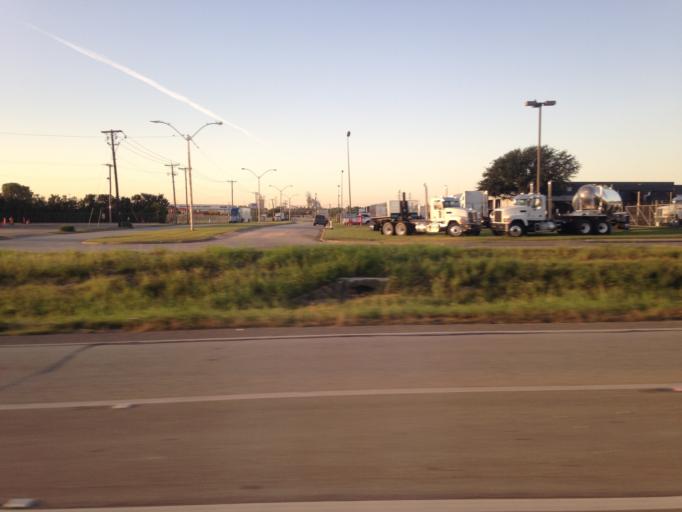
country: US
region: Texas
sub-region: Tarrant County
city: Blue Mound
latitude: 32.8421
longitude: -97.3386
